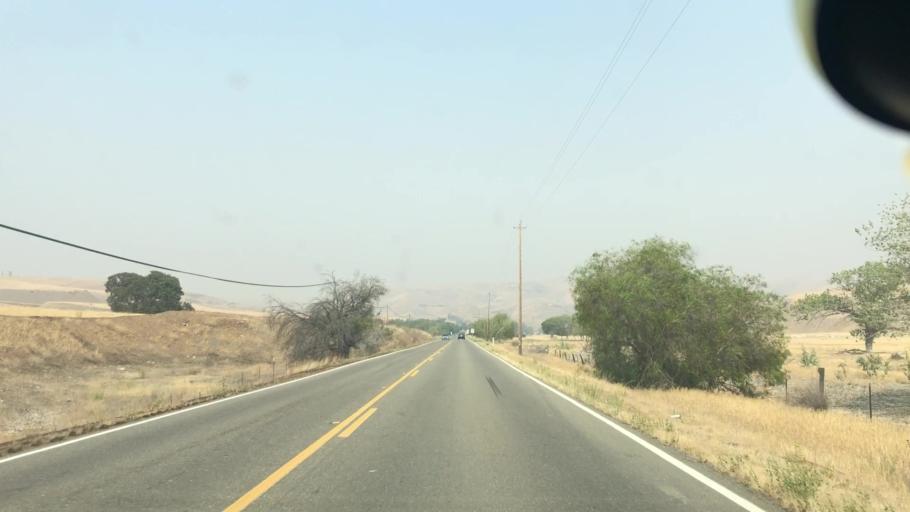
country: US
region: California
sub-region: San Joaquin County
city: Tracy
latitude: 37.6304
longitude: -121.5113
